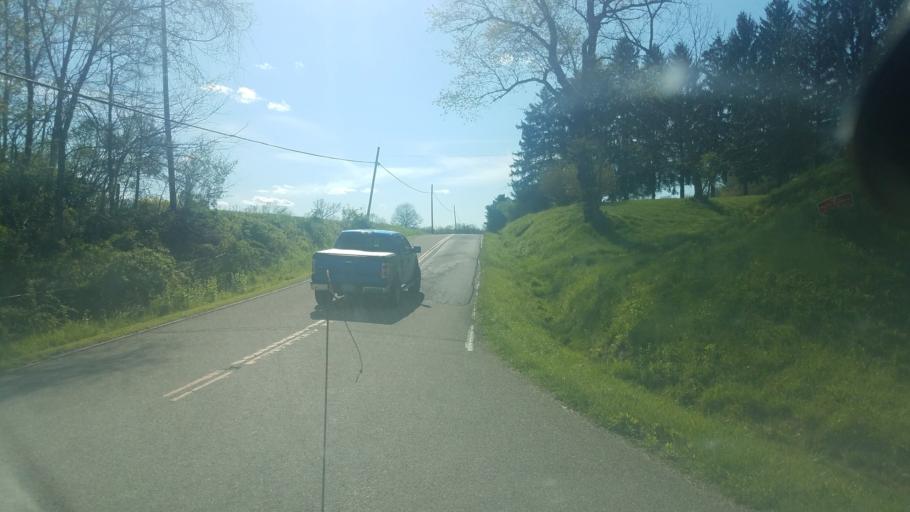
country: US
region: Ohio
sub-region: Coshocton County
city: Coshocton
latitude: 40.3401
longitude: -81.9288
